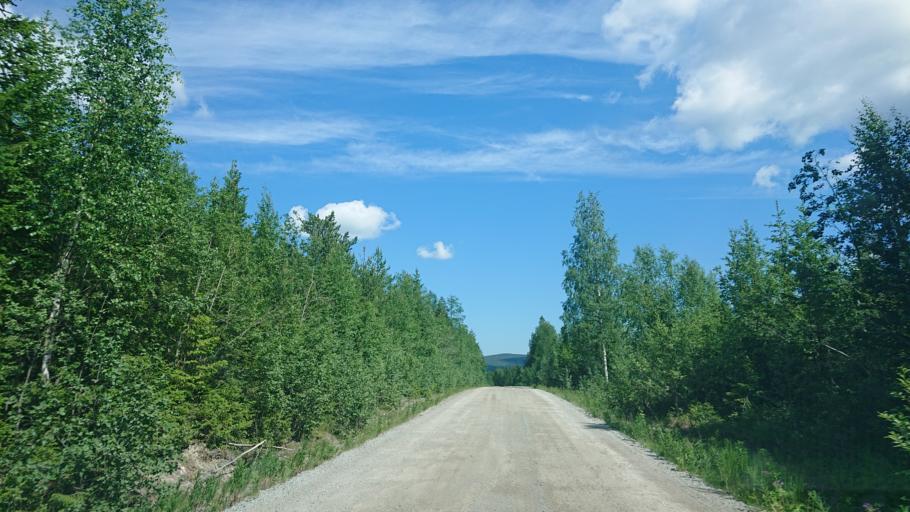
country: SE
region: Vaesternorrland
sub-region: Solleftea Kommun
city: Solleftea
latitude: 62.9449
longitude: 17.1257
